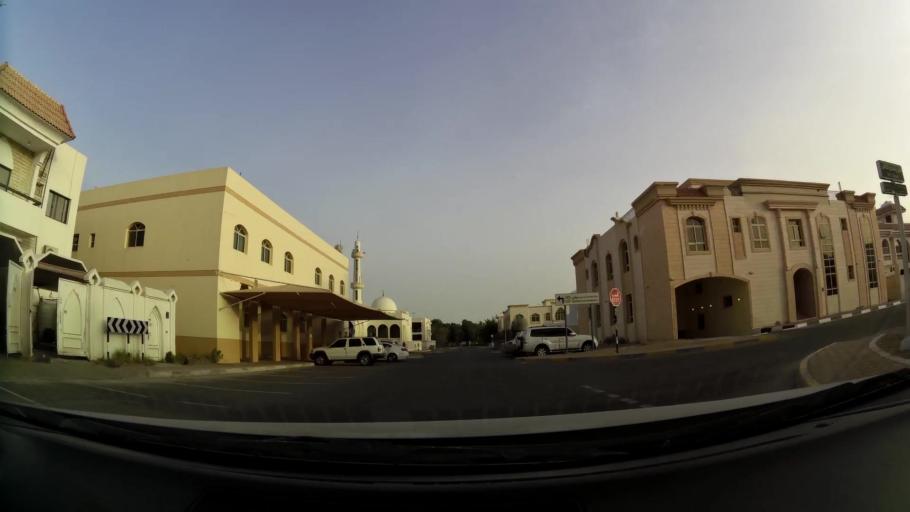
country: AE
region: Abu Dhabi
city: Al Ain
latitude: 24.2442
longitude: 55.7219
